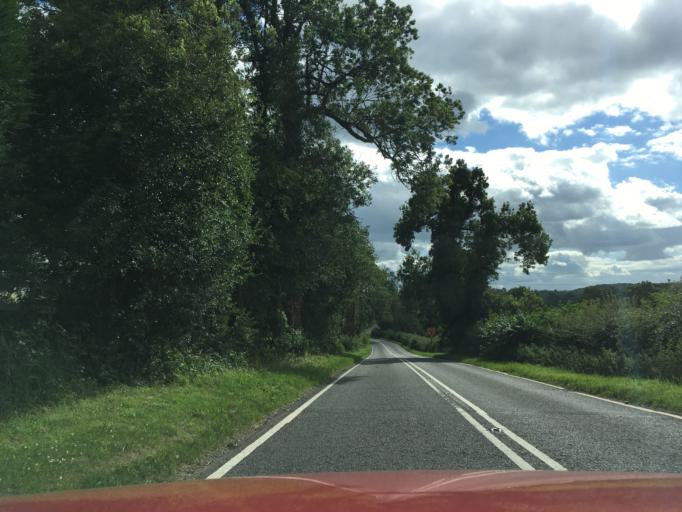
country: GB
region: England
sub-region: Leicestershire
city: Coalville
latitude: 52.7673
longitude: -1.3911
